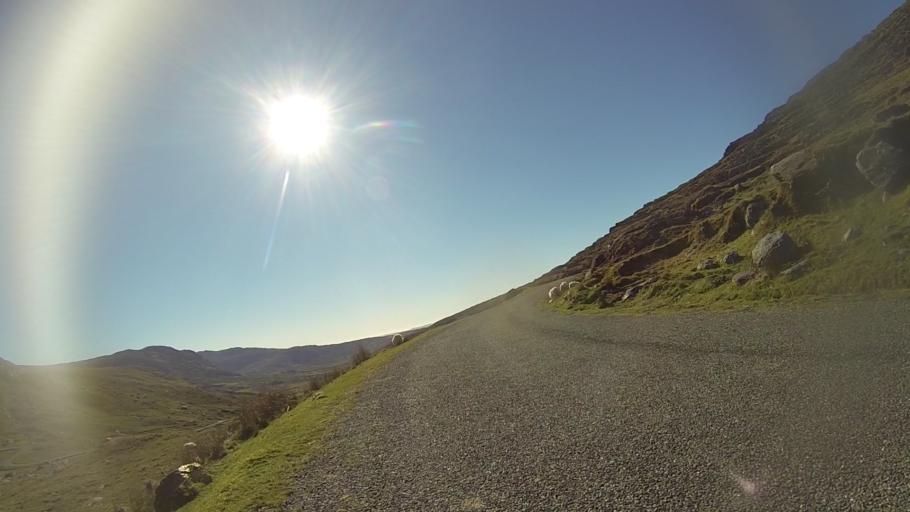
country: IE
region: Munster
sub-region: Ciarrai
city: Kenmare
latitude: 51.7195
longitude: -9.7539
